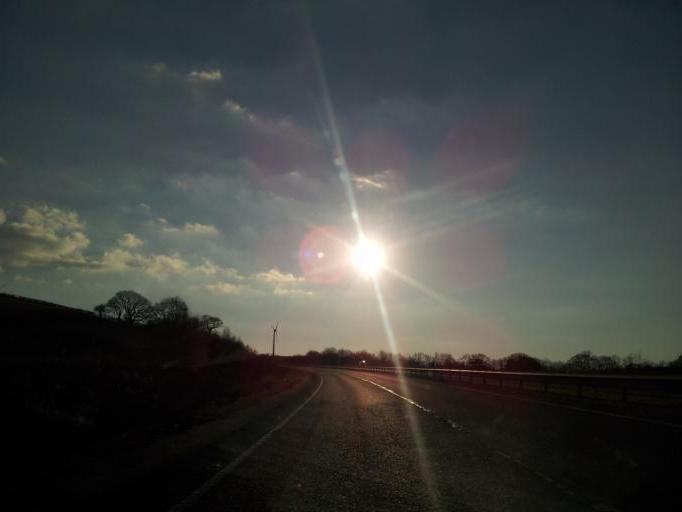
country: GB
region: England
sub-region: Cornwall
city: Launceston
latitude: 50.6670
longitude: -4.2678
